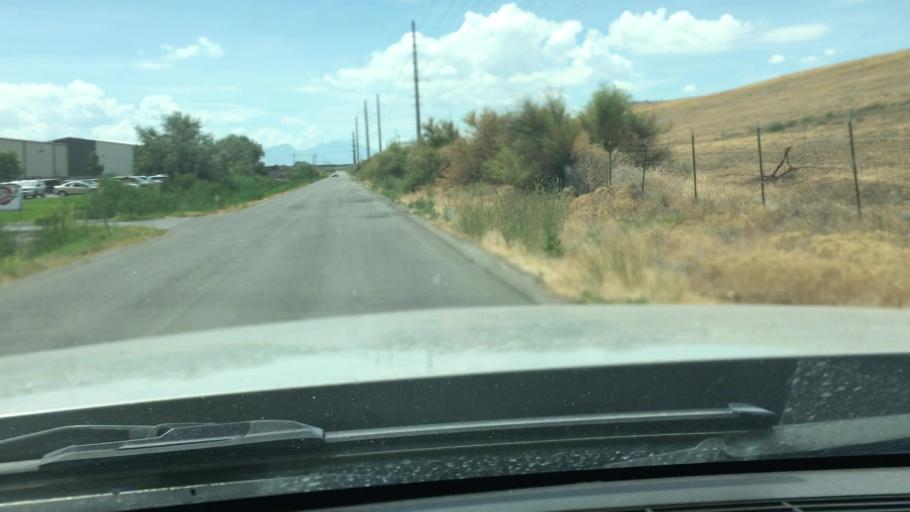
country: US
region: Utah
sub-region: Utah County
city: Pleasant Grove
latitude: 40.3372
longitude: -111.7599
